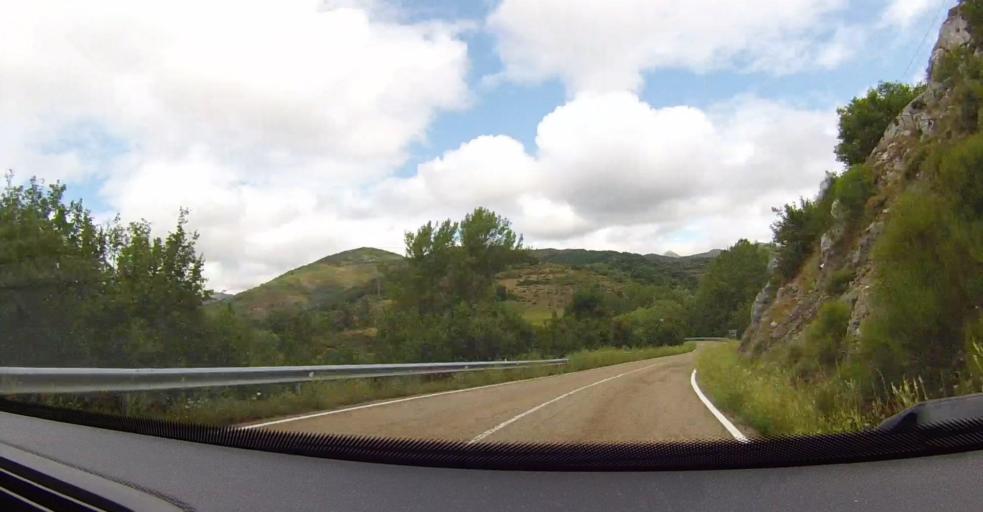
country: ES
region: Castille and Leon
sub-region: Provincia de Leon
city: Puebla de Lillo
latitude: 42.9772
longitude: -5.2567
